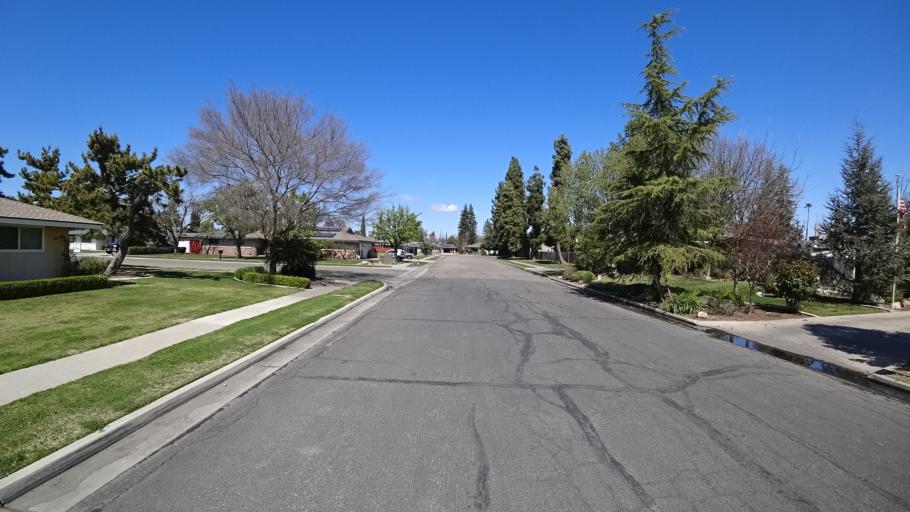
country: US
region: California
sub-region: Fresno County
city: Fresno
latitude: 36.8208
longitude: -119.8016
